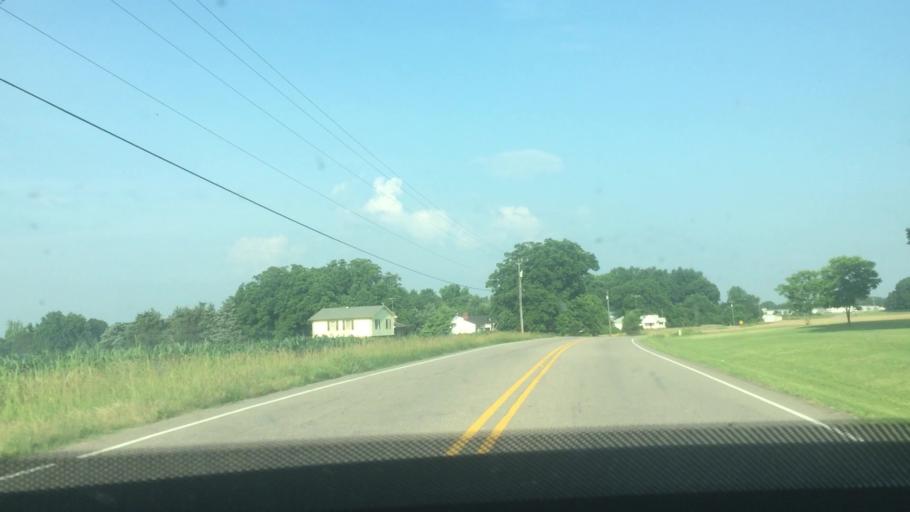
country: US
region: North Carolina
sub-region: Rowan County
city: Enochville
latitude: 35.5814
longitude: -80.7276
